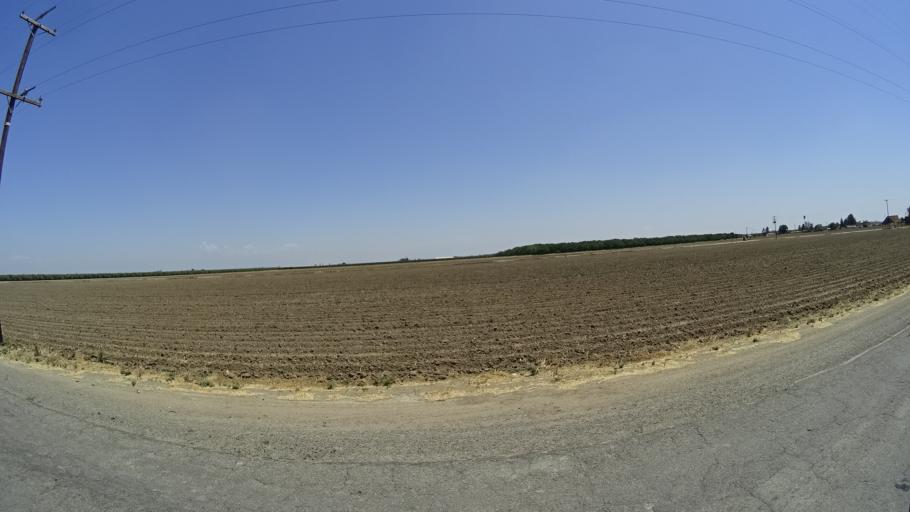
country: US
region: California
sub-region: Kings County
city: Armona
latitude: 36.3618
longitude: -119.7270
